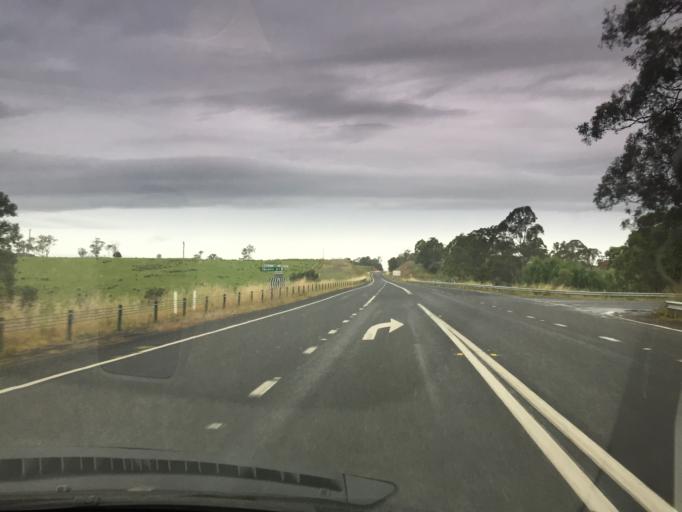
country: AU
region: New South Wales
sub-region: Bega Valley
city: Bega
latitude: -36.6440
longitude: 149.5868
